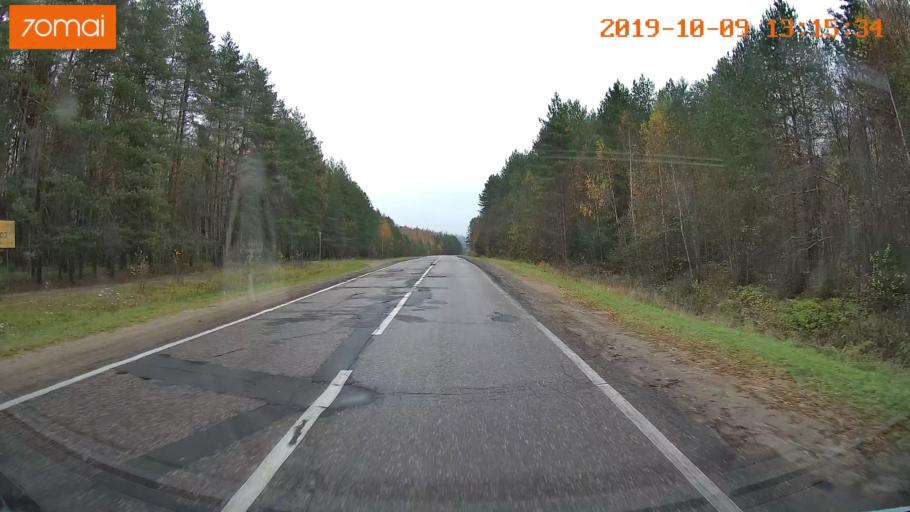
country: RU
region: Jaroslavl
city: Lyubim
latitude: 58.3669
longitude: 40.7539
